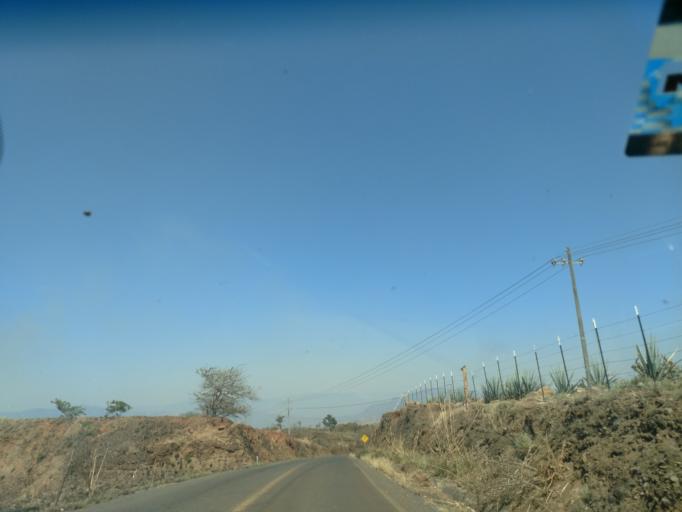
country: MX
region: Nayarit
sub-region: Tepic
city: La Corregidora
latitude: 21.4931
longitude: -104.6877
